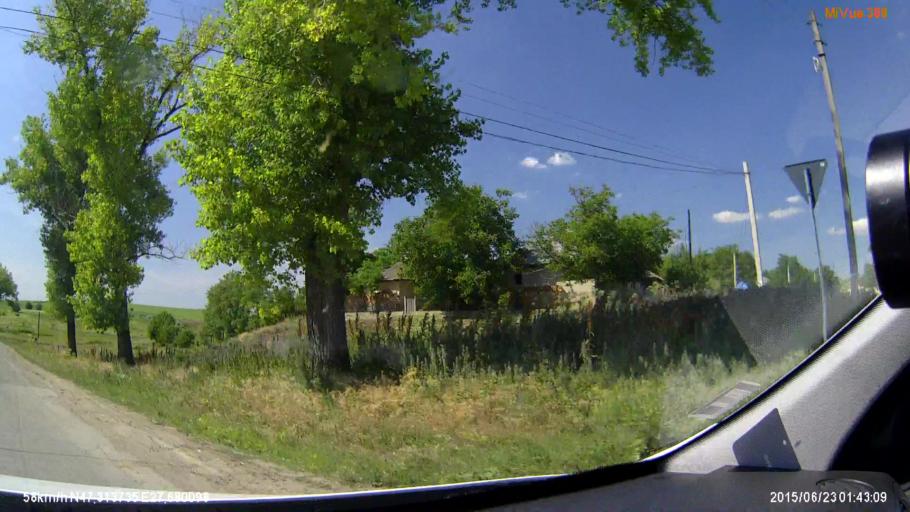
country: RO
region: Iasi
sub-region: Comuna Golaesti
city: Golaesti
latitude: 47.3137
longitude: 27.6803
